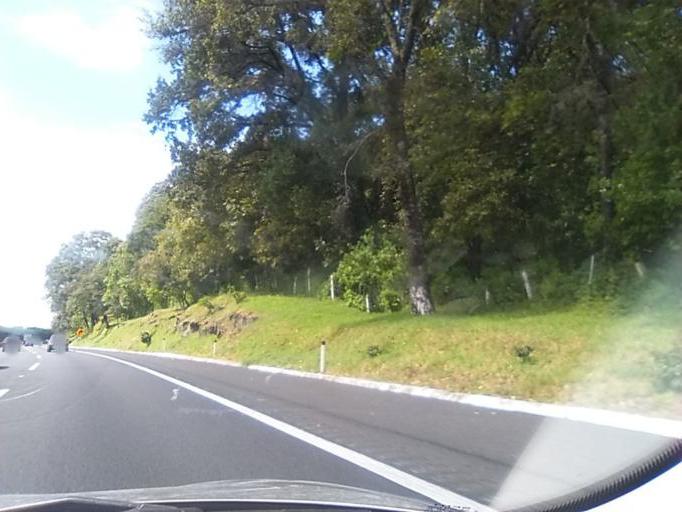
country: MX
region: Morelos
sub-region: Cuernavaca
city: Villa Santiago
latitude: 19.0007
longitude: -99.1915
